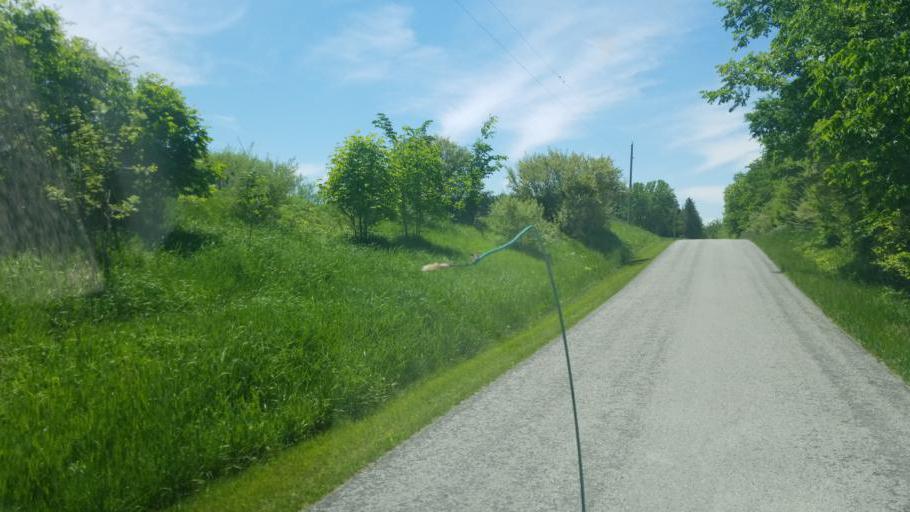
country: US
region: Ohio
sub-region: Huron County
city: Willard
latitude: 41.1203
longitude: -82.7094
